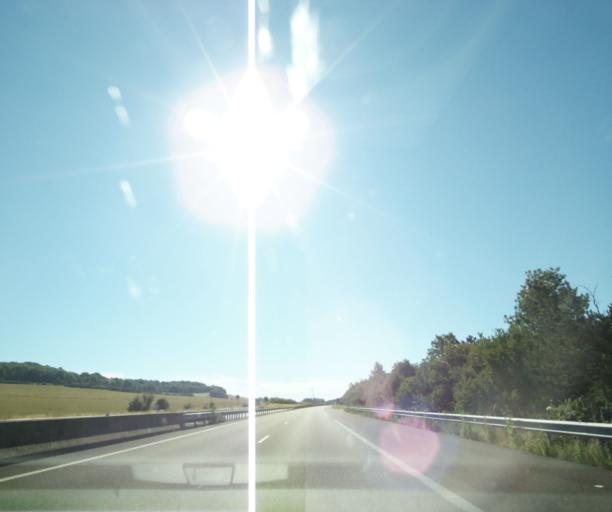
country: FR
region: Champagne-Ardenne
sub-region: Departement de la Haute-Marne
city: Nogent-le-Bas
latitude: 47.9565
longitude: 5.4121
